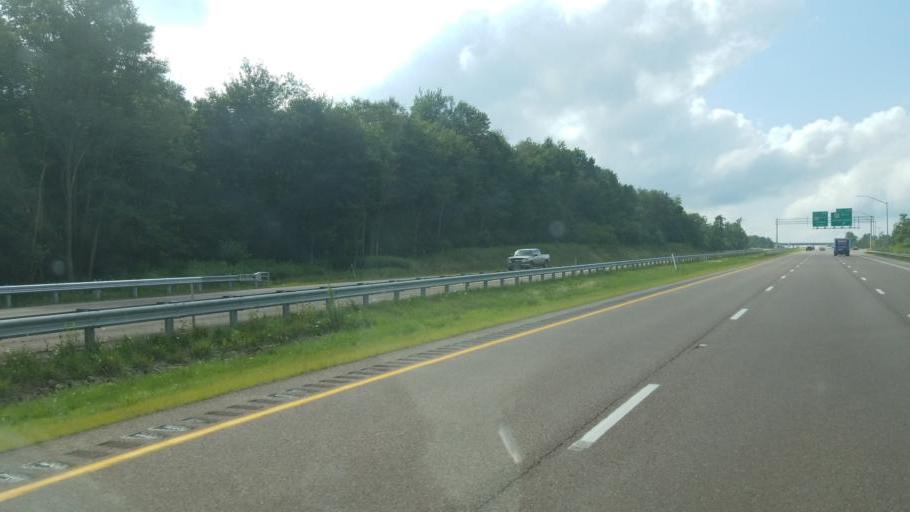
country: US
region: Pennsylvania
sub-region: Somerset County
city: Meyersdale
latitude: 39.6827
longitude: -79.2394
